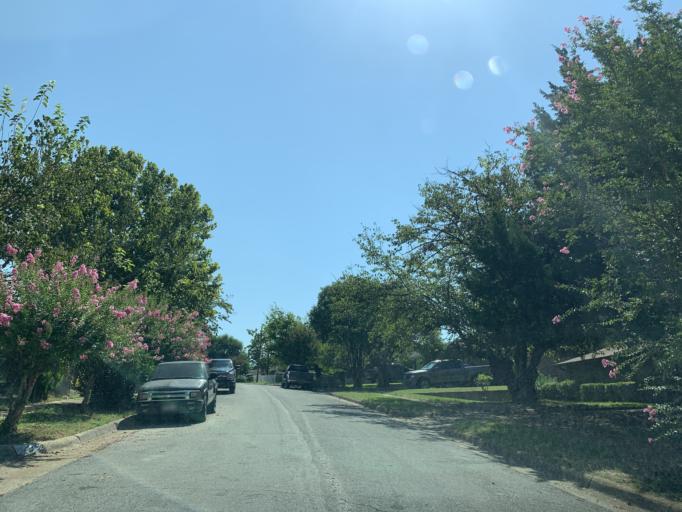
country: US
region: Texas
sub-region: Dallas County
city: Hutchins
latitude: 32.6684
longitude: -96.7483
